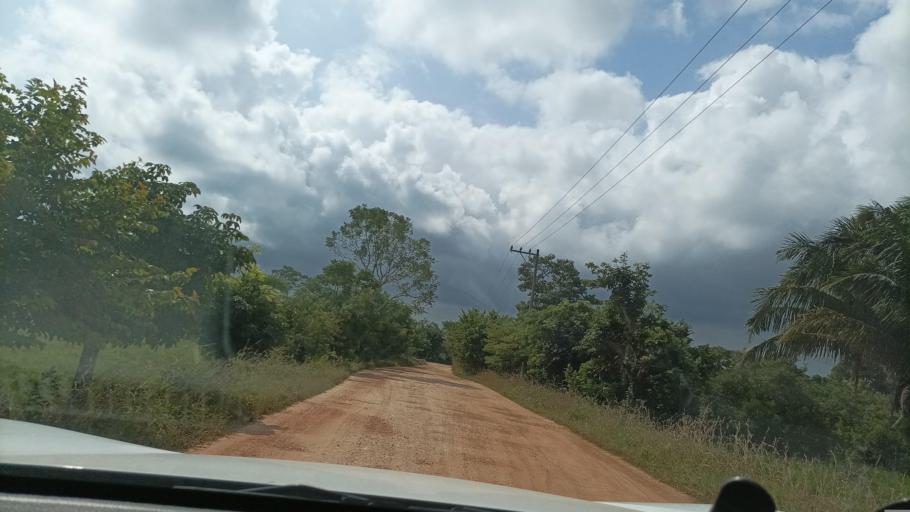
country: MX
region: Veracruz
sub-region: Chinameca
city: Chacalapa
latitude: 18.0826
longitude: -94.6758
